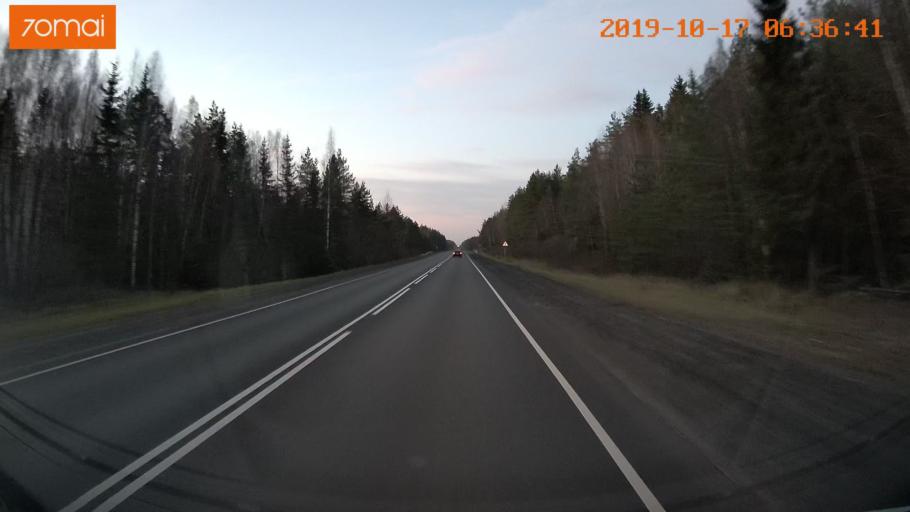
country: RU
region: Ivanovo
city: Novoye Leushino
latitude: 56.6788
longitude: 40.6027
